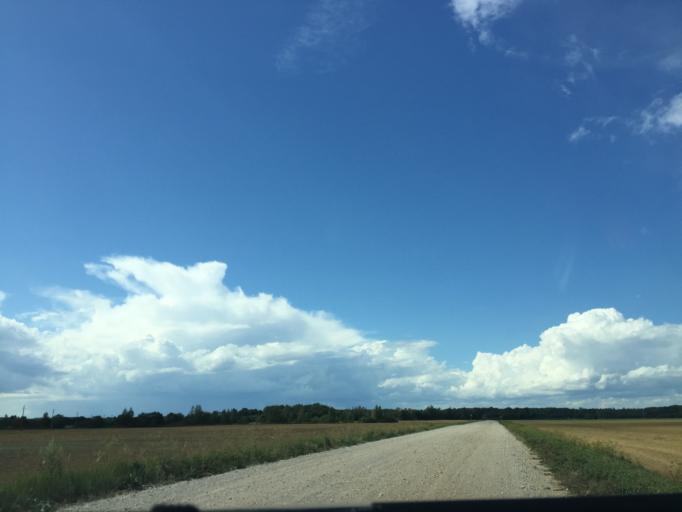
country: LT
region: Siauliu apskritis
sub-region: Joniskis
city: Joniskis
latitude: 56.3241
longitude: 23.5878
